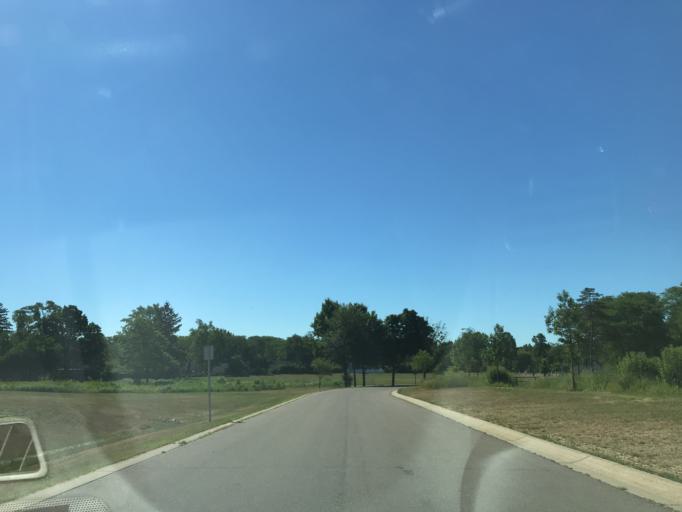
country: US
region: Michigan
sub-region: Washtenaw County
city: Ann Arbor
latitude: 42.2480
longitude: -83.7107
